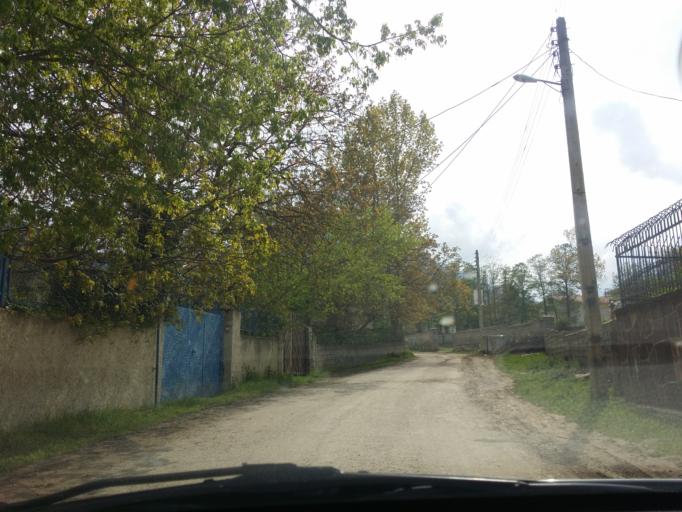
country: IR
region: Mazandaran
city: `Abbasabad
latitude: 36.4963
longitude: 51.1486
